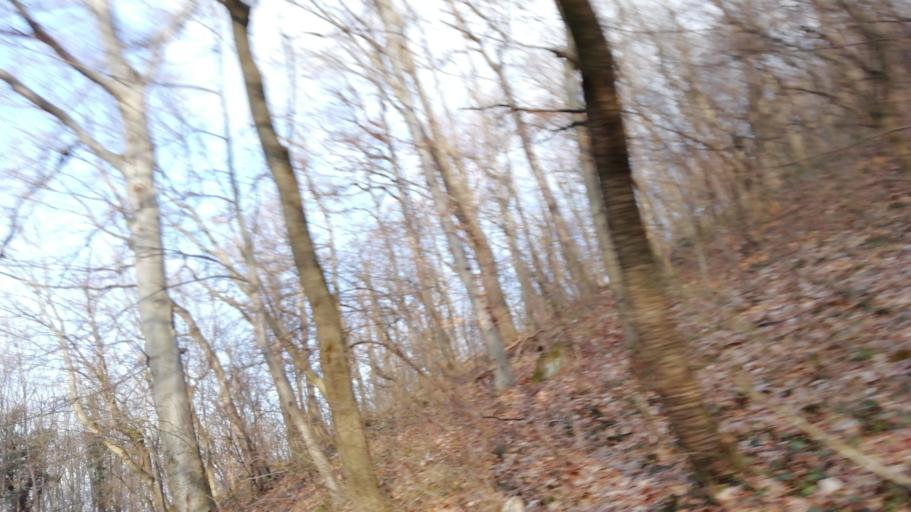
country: HU
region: Pest
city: Budakeszi
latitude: 47.5356
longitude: 18.9515
